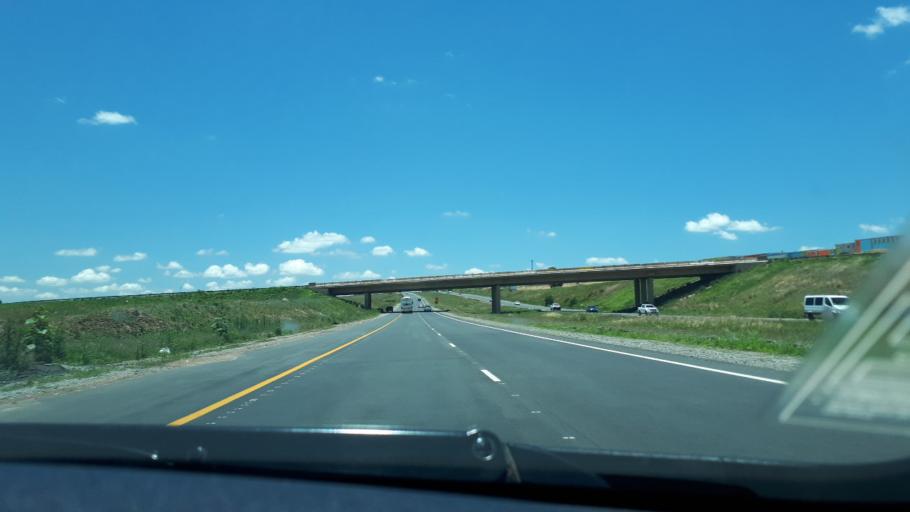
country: ZA
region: Gauteng
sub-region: City of Johannesburg Metropolitan Municipality
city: Diepsloot
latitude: -25.9310
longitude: 27.9916
